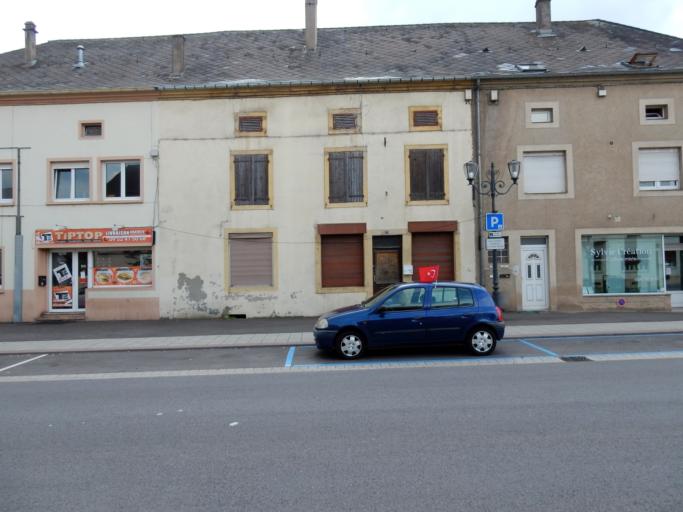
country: FR
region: Lorraine
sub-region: Departement de la Moselle
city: Uckange
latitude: 49.3020
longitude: 6.1578
